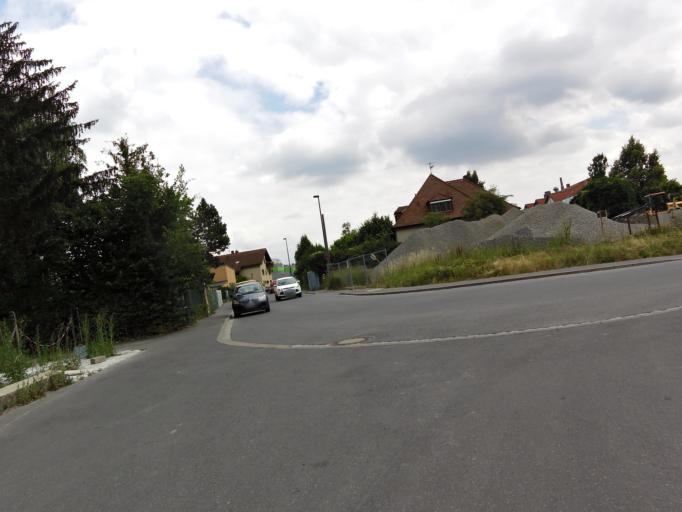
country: DE
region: Bavaria
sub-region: Regierungsbezirk Unterfranken
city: Wuerzburg
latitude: 49.7692
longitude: 9.9404
